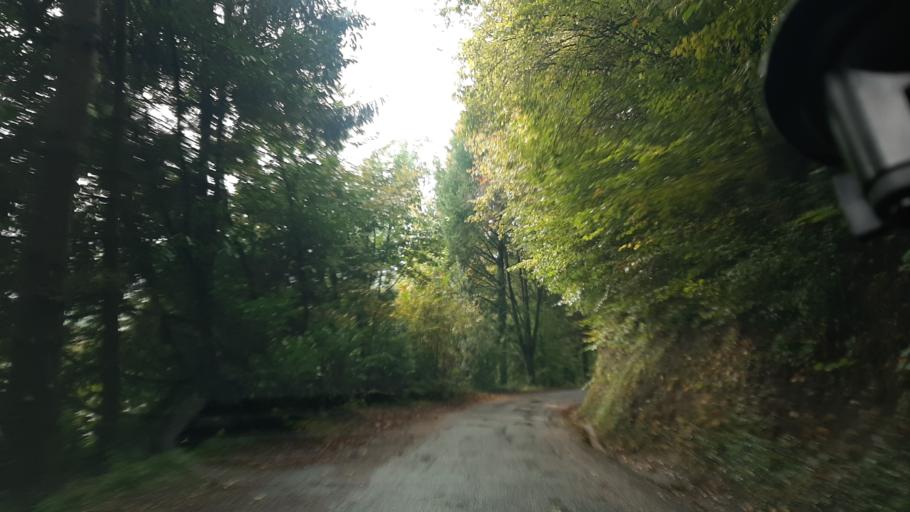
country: FR
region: Rhone-Alpes
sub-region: Departement de la Savoie
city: Gresy-sur-Isere
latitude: 45.6196
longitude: 6.2752
